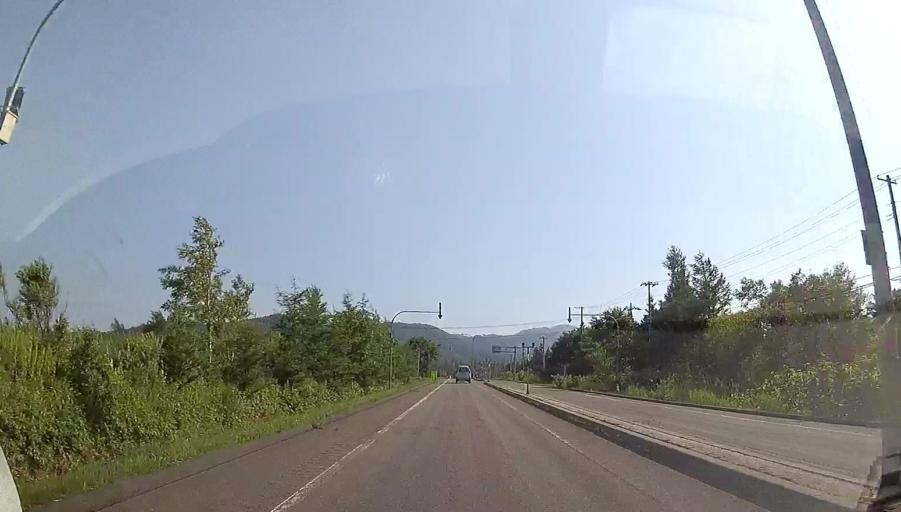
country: JP
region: Hokkaido
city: Otofuke
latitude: 42.9870
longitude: 142.8392
